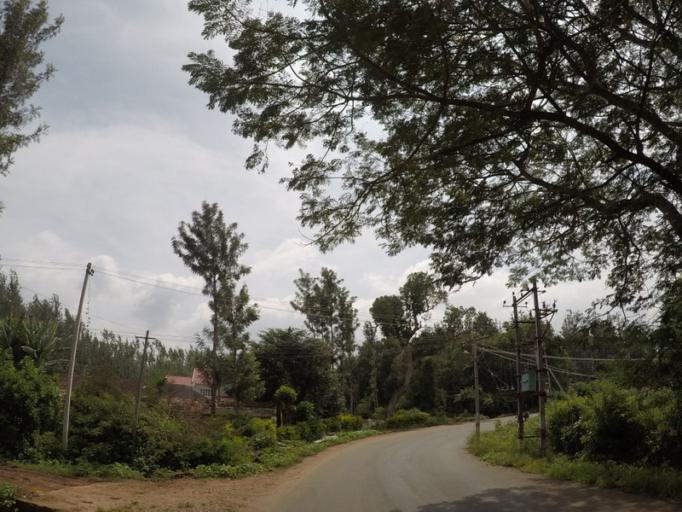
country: IN
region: Karnataka
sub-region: Chikmagalur
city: Chikmagalur
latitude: 13.4037
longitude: 75.7962
